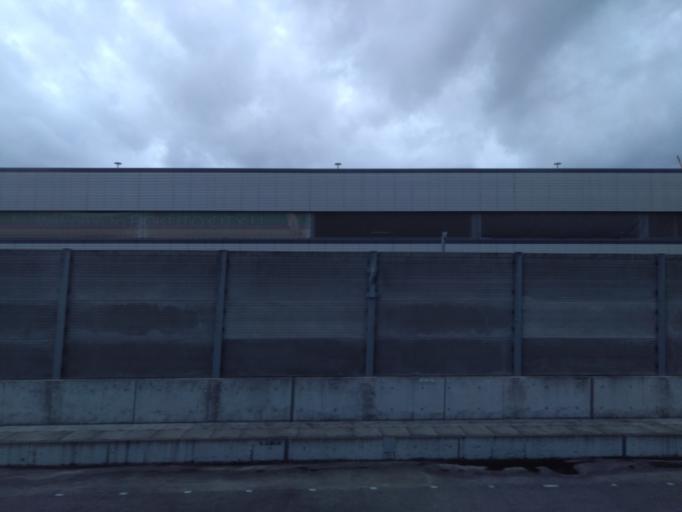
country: JP
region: Hokkaido
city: Nanae
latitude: 41.9041
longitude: 140.6505
